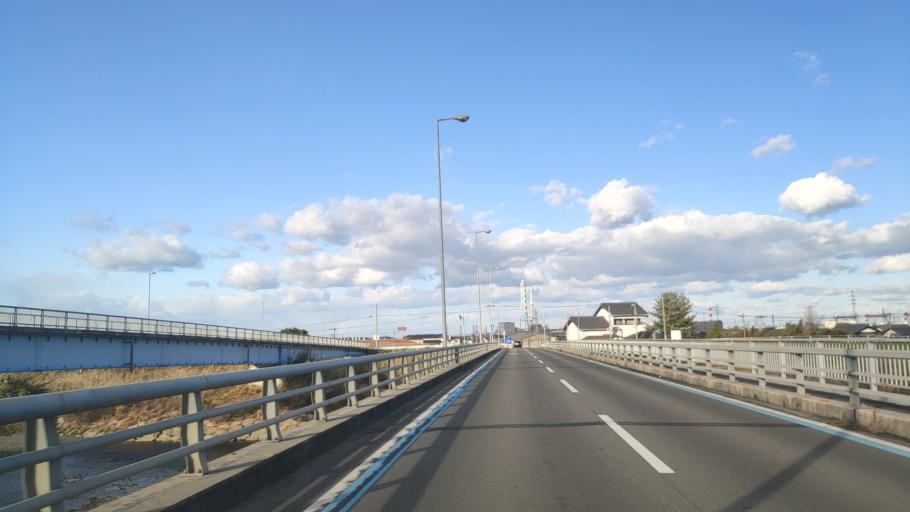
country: JP
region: Ehime
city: Saijo
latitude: 33.9127
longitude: 133.1616
